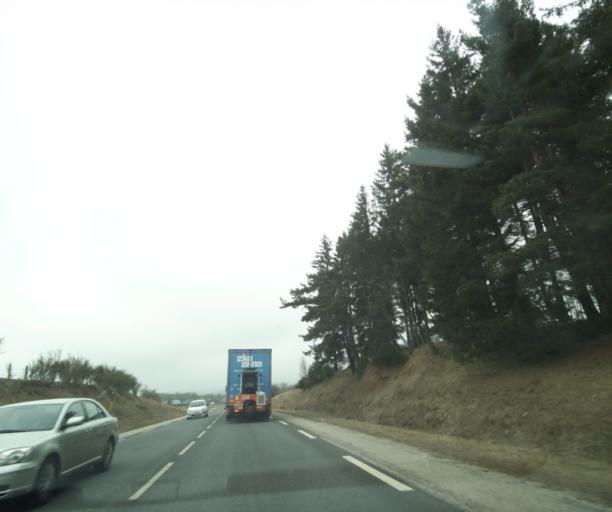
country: FR
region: Languedoc-Roussillon
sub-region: Departement de la Lozere
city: Langogne
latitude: 44.7069
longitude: 3.8212
